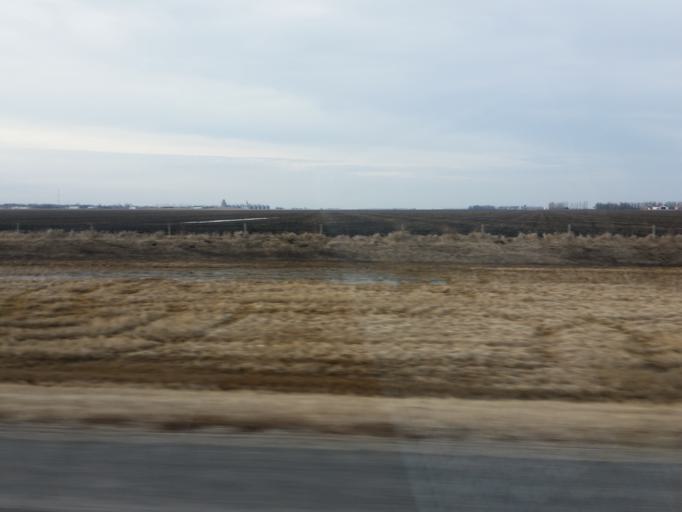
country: US
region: North Dakota
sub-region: Cass County
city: Casselton
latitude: 46.8768
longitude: -97.1870
